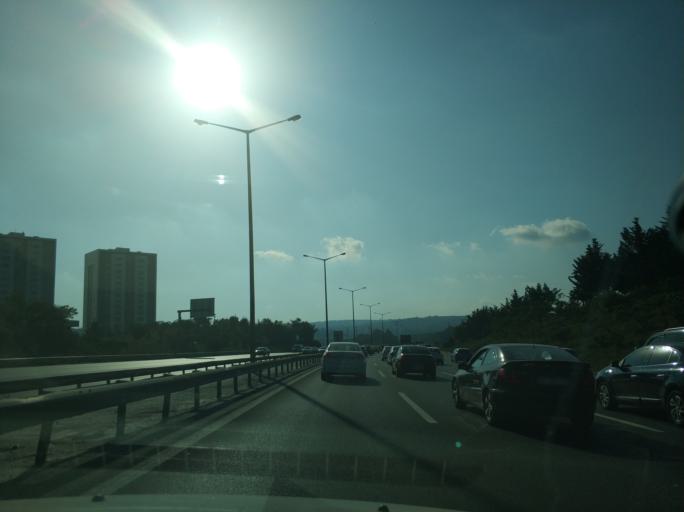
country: TR
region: Istanbul
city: Sisli
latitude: 41.0919
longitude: 28.9392
